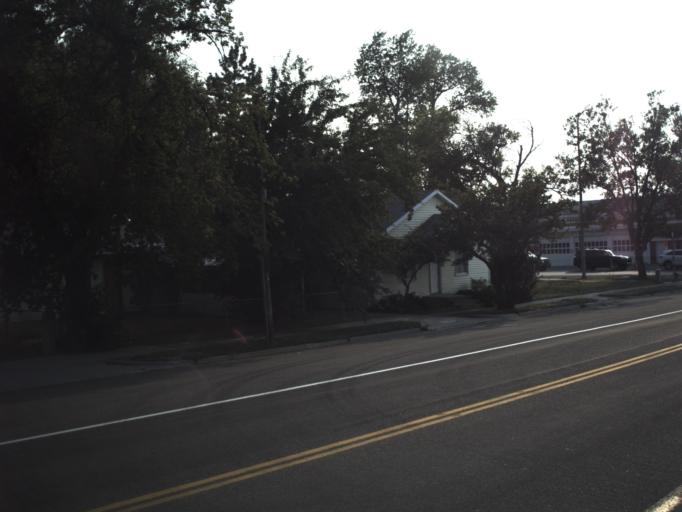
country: US
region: Utah
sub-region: Summit County
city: Kamas
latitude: 40.6432
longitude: -111.2799
